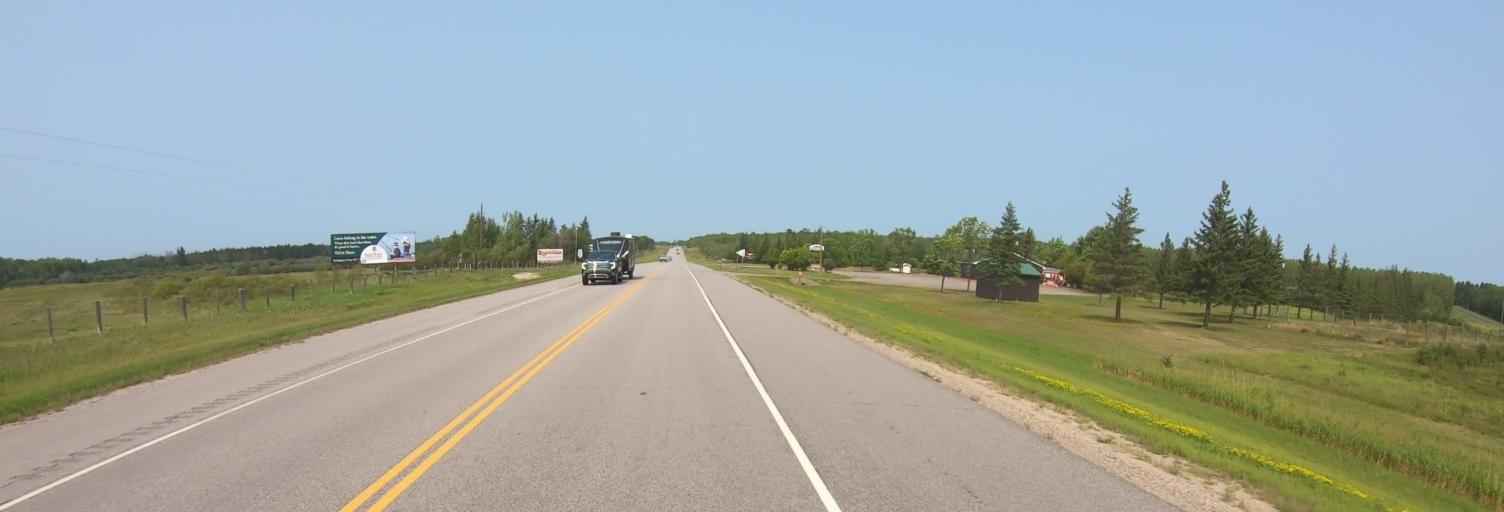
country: CA
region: Ontario
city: Fort Frances
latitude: 48.4126
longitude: -93.2056
